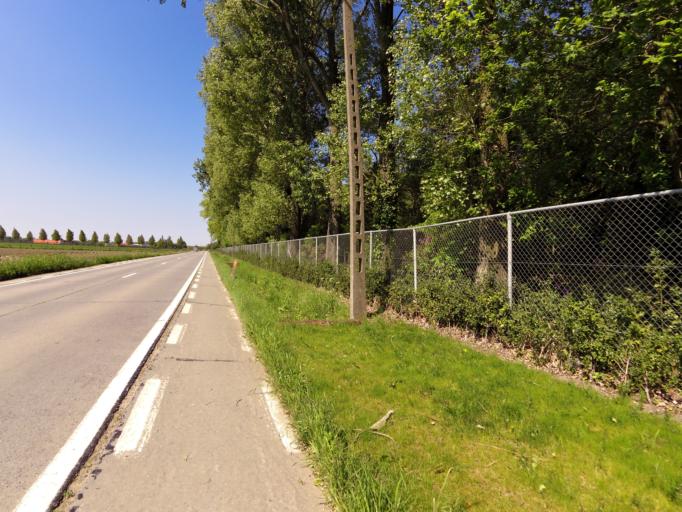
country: BE
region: Flanders
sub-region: Provincie West-Vlaanderen
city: Koekelare
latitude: 51.0607
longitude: 2.9391
